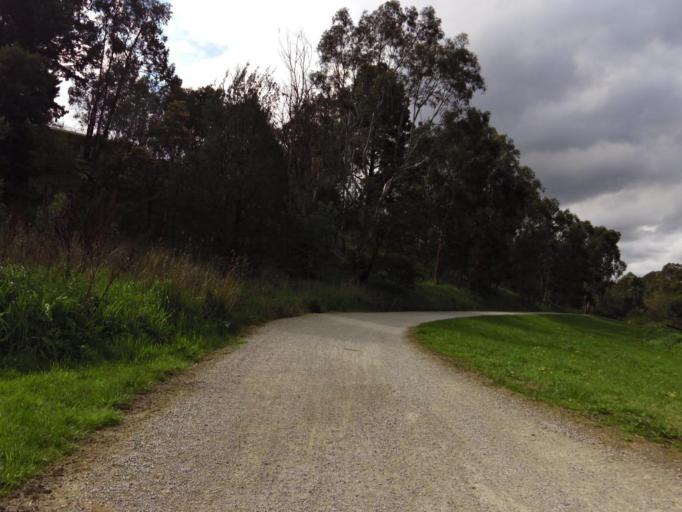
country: AU
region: Victoria
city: Ivanhoe East
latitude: -37.7811
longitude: 145.0652
